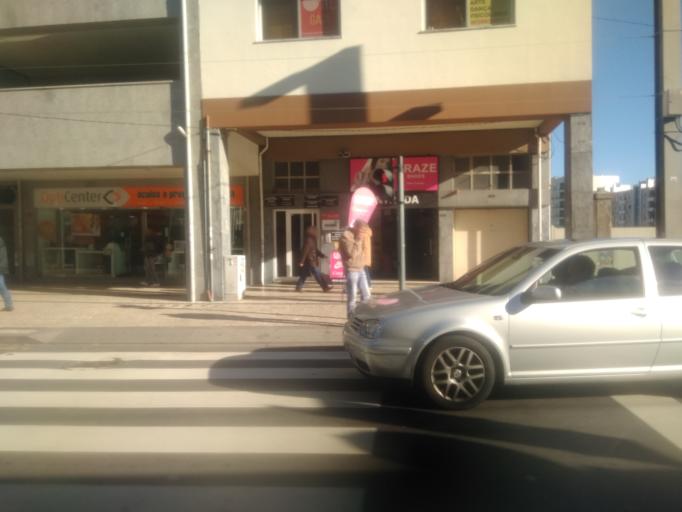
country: PT
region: Porto
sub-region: Vila Nova de Gaia
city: Vila Nova de Gaia
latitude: 41.1265
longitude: -8.6054
